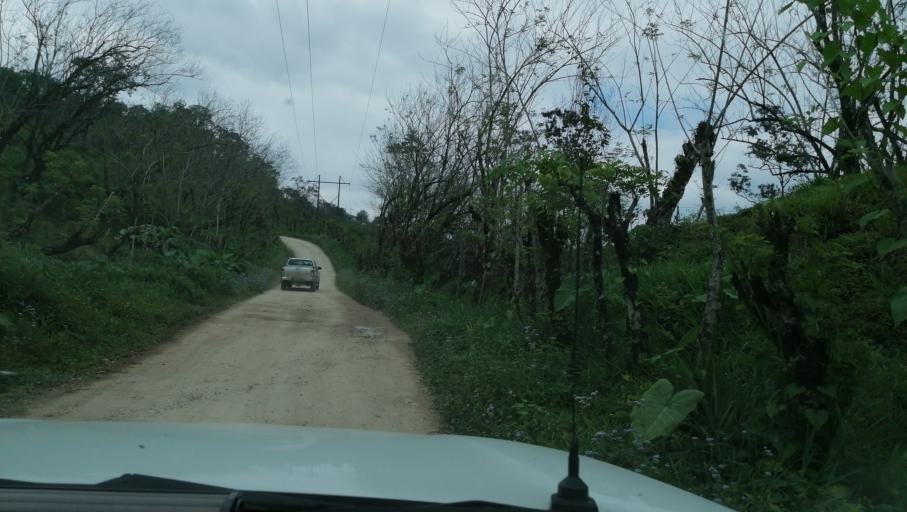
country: MX
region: Chiapas
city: Ocotepec
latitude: 17.2755
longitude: -93.2258
